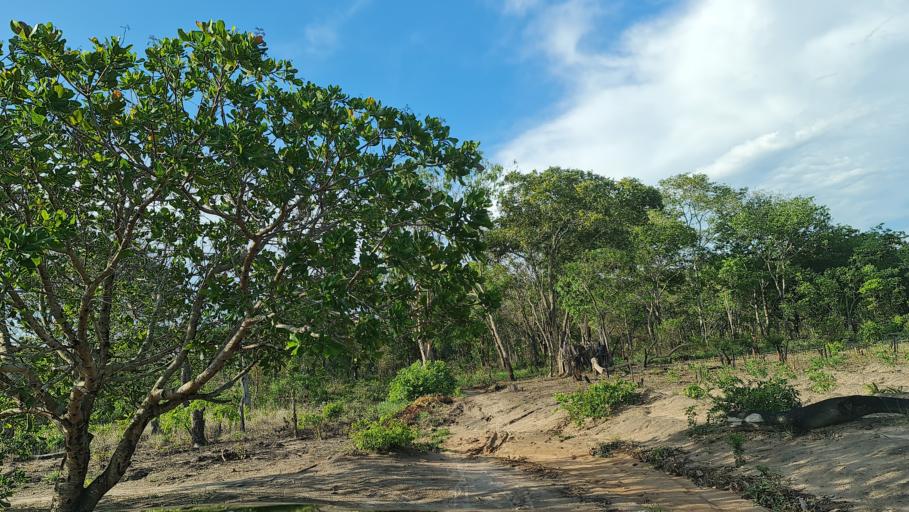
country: MZ
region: Zambezia
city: Quelimane
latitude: -17.1945
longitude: 37.4163
